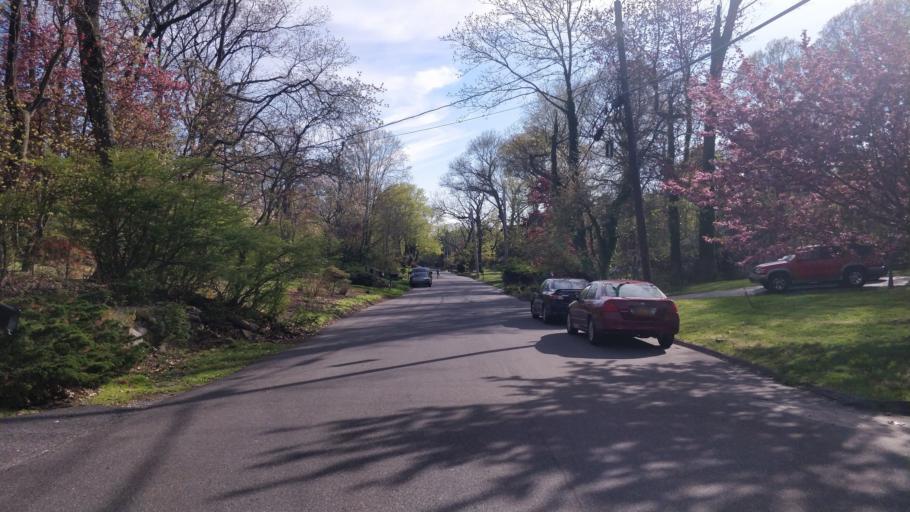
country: US
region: New York
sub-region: Suffolk County
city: Stony Brook
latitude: 40.9384
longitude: -73.1312
